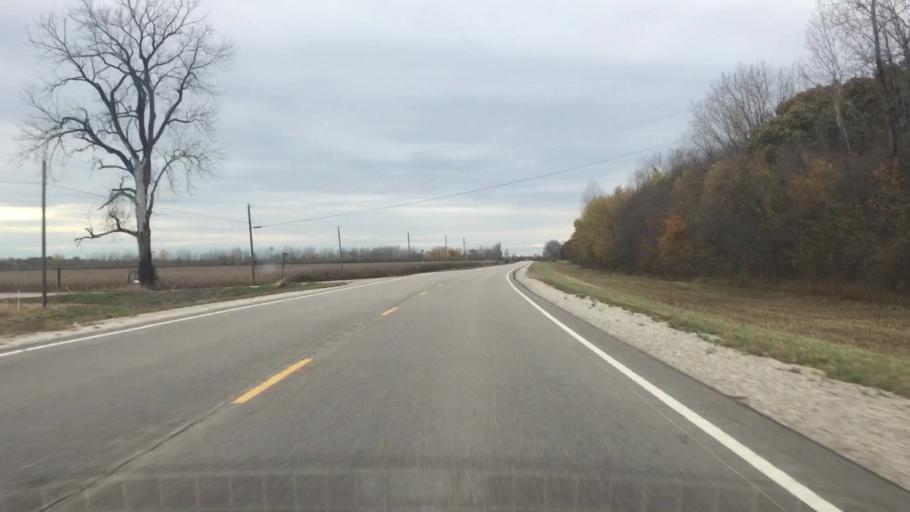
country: US
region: Missouri
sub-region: Callaway County
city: Holts Summit
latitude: 38.5807
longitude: -92.0995
